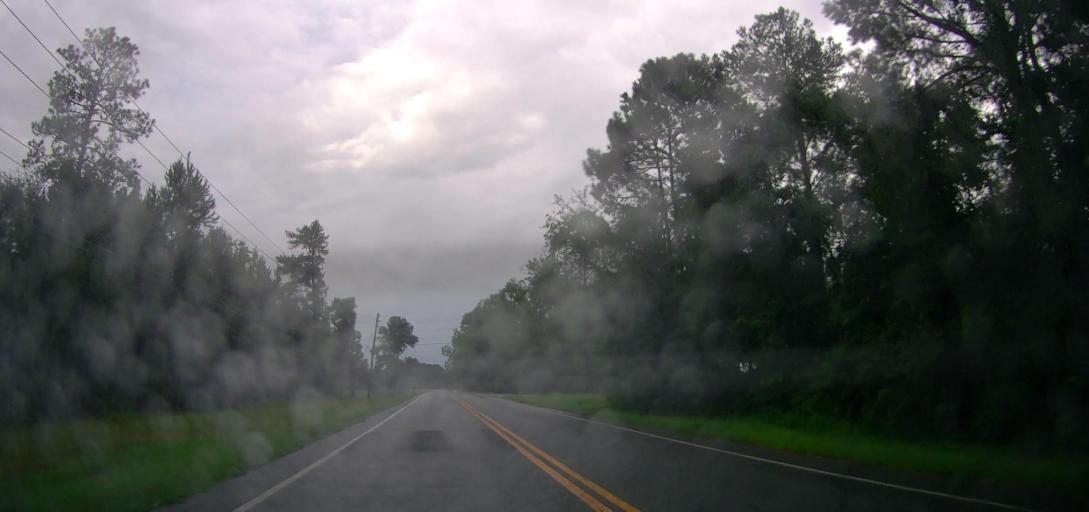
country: US
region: Georgia
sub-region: Ware County
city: Deenwood
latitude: 31.1956
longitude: -82.3825
